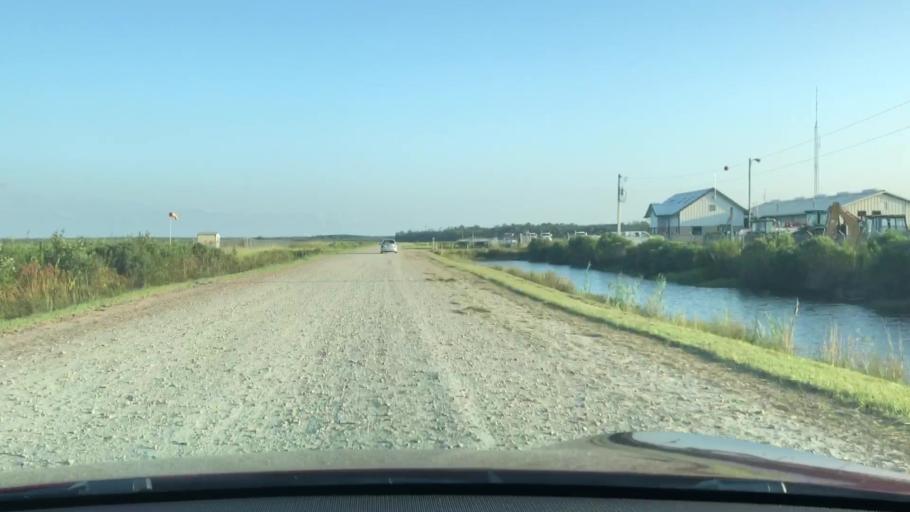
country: US
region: North Carolina
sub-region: Dare County
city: Manteo
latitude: 35.8556
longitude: -75.8625
